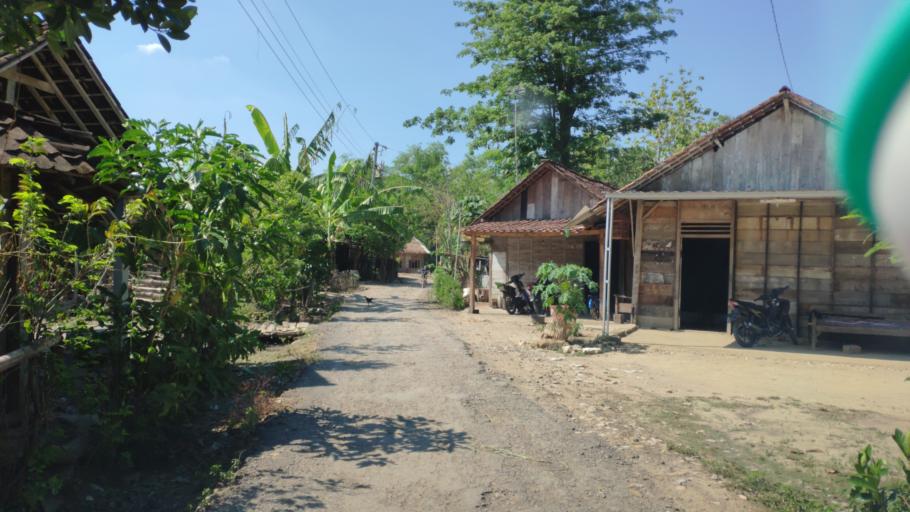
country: ID
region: Central Java
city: Botoh
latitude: -7.0871
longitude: 111.4666
